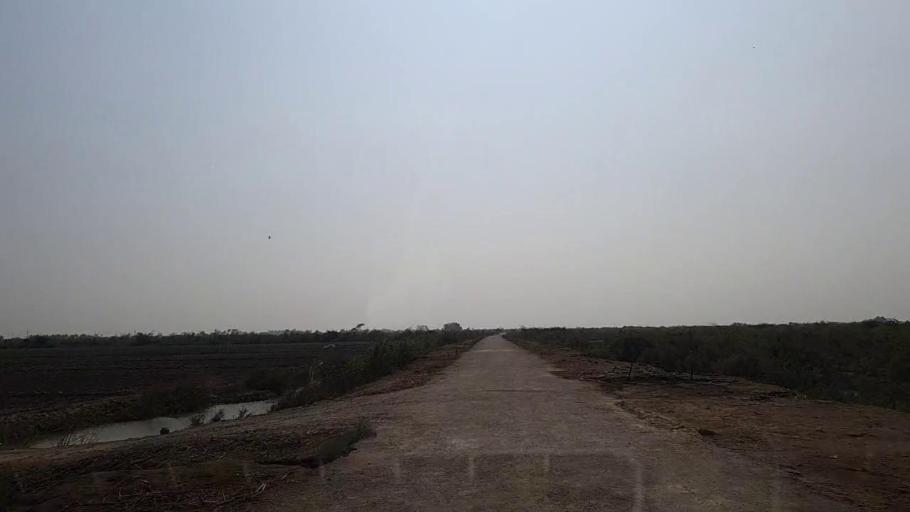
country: PK
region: Sindh
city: Mirpur Sakro
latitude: 24.6574
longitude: 67.6920
